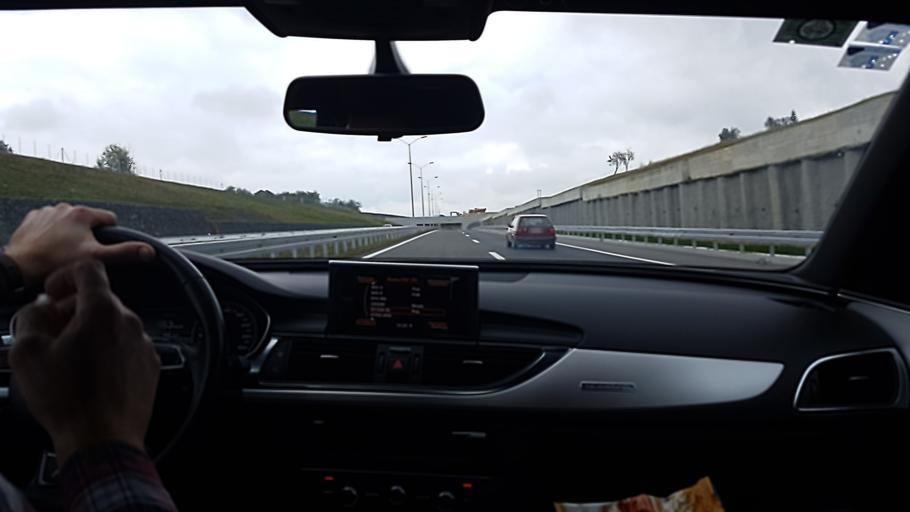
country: BA
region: Republika Srpska
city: Prnjavor
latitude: 44.8517
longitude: 17.7272
